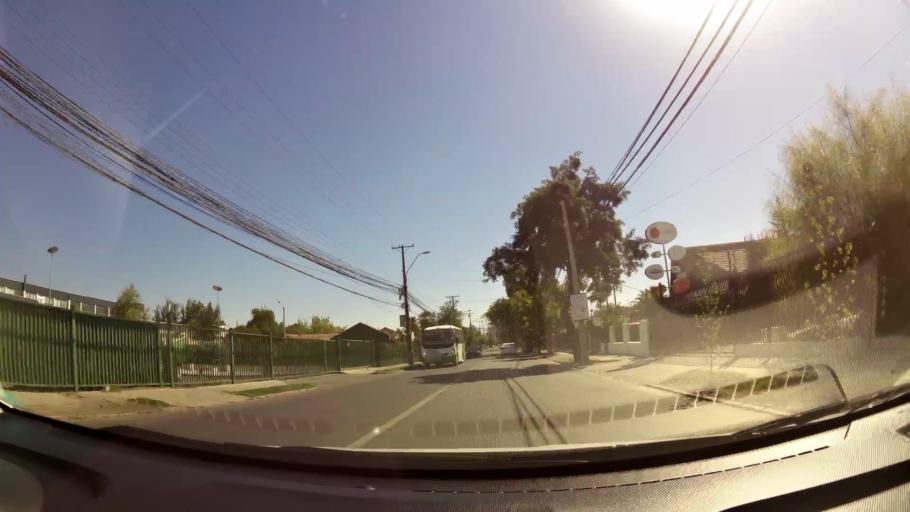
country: CL
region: O'Higgins
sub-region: Provincia de Cachapoal
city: Rancagua
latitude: -34.1784
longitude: -70.7442
